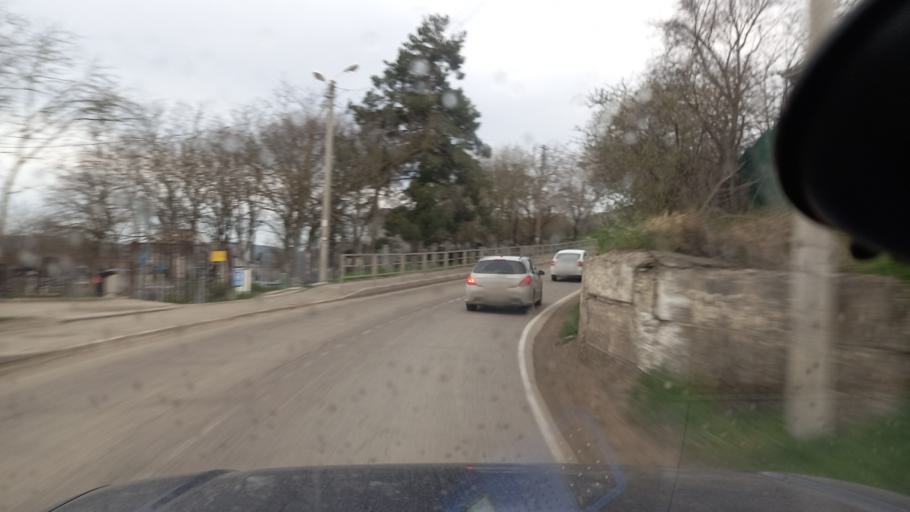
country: RU
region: Krasnodarskiy
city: Anapskaya
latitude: 44.8435
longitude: 37.3808
